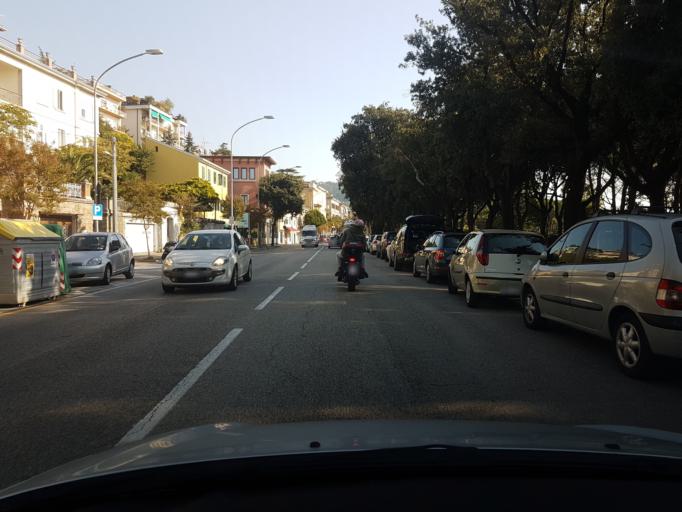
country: IT
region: Friuli Venezia Giulia
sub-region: Provincia di Trieste
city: Prosecco-Contovello
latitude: 45.6857
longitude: 13.7482
